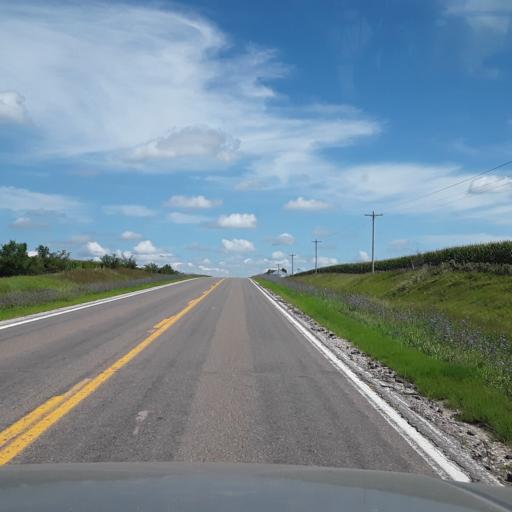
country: US
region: Nebraska
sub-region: York County
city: York
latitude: 40.9896
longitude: -97.4062
